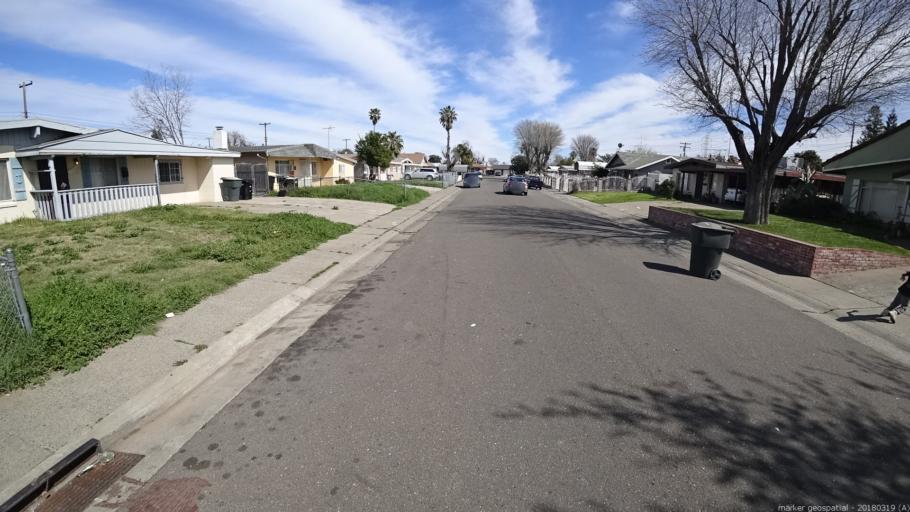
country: US
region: California
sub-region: Sacramento County
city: Parkway
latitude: 38.5097
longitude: -121.4395
